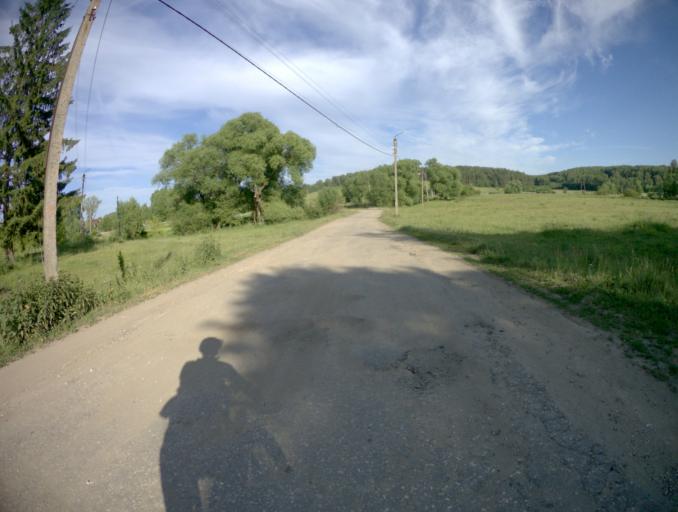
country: RU
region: Vladimir
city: Vorsha
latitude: 56.1712
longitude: 40.1633
